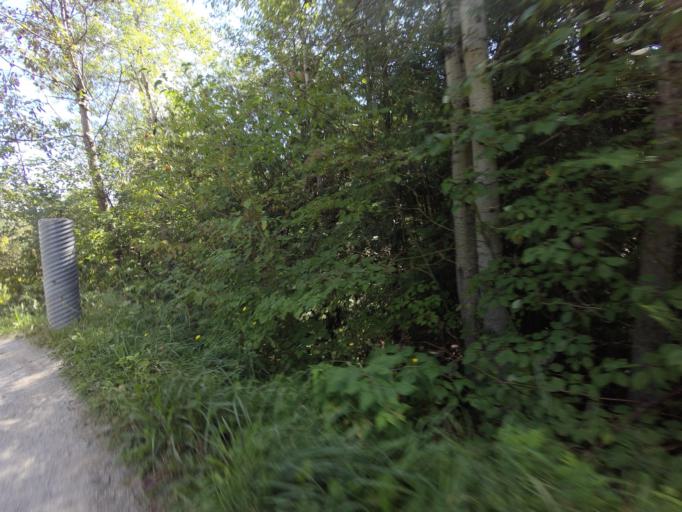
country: CA
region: Ontario
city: Orangeville
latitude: 43.7744
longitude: -80.0973
